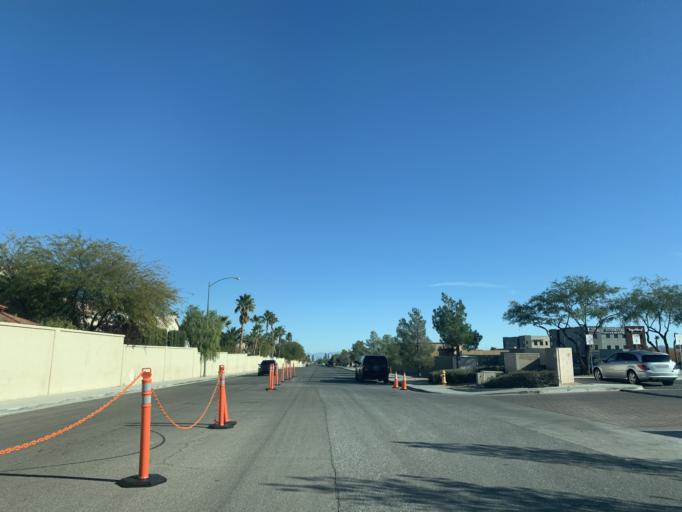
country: US
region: Nevada
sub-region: Clark County
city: Summerlin South
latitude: 36.1168
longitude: -115.3020
